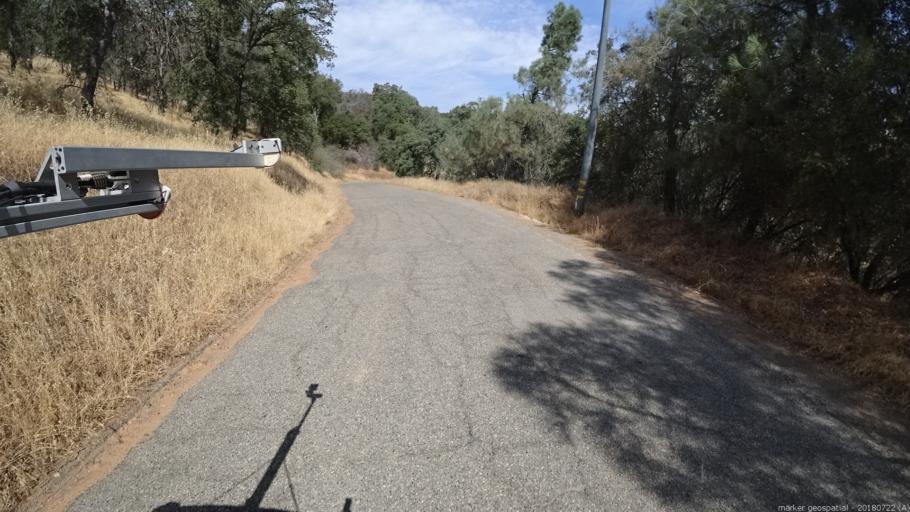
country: US
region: California
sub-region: Madera County
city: Coarsegold
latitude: 37.2619
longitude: -119.7085
